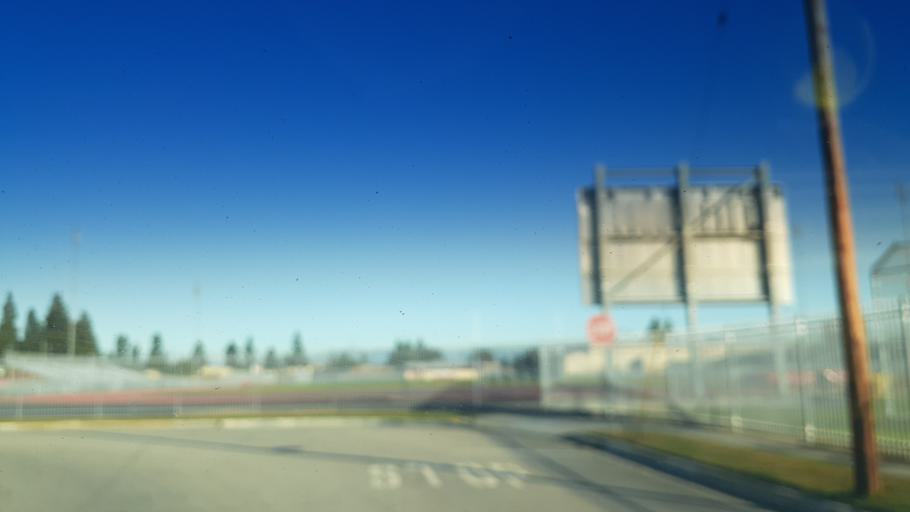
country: US
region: California
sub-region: Los Angeles County
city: Hawaiian Gardens
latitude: 33.8429
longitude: -118.0764
